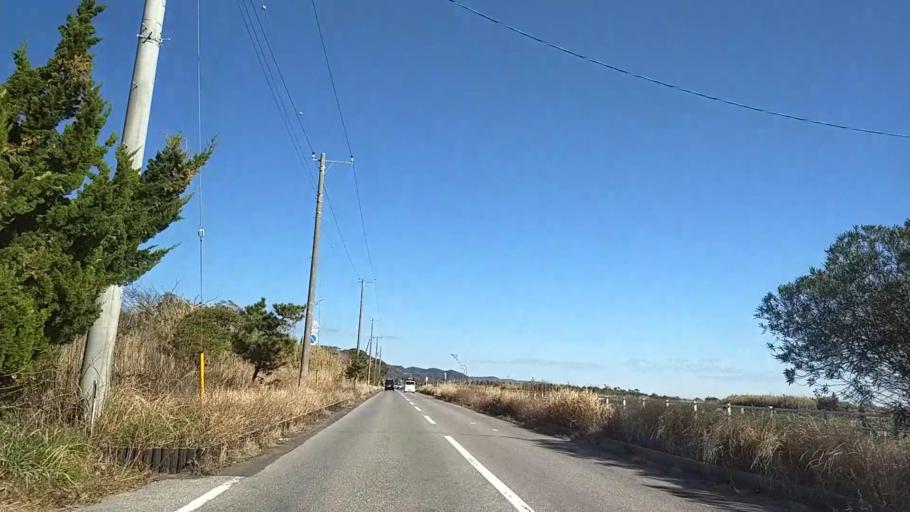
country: JP
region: Chiba
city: Tateyama
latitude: 35.0112
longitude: 139.9785
